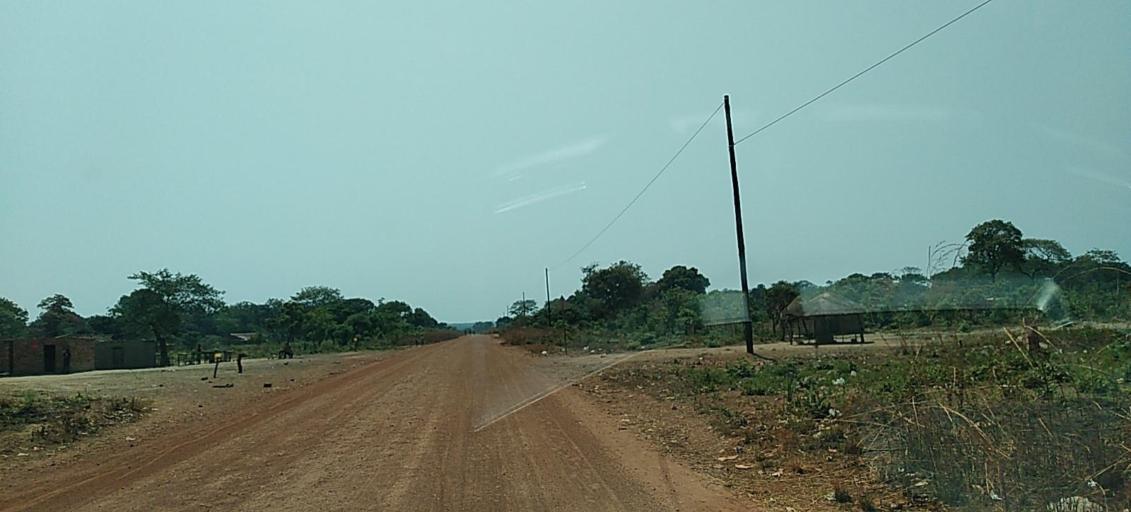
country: ZM
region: North-Western
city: Kansanshi
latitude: -11.9971
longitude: 26.6062
